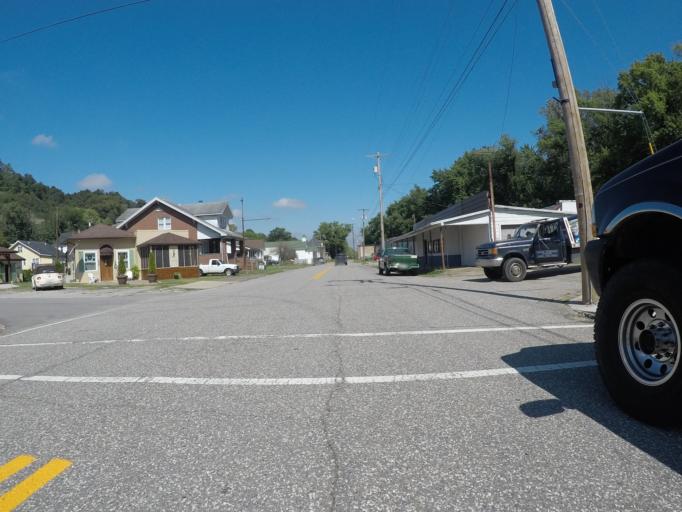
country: US
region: Ohio
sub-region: Lawrence County
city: South Point
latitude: 38.4219
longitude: -82.5994
